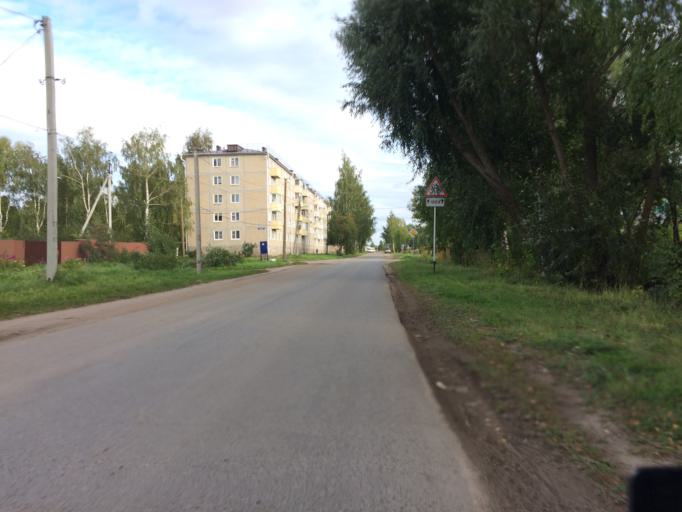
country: RU
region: Mariy-El
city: Yoshkar-Ola
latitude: 56.6576
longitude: 48.0056
